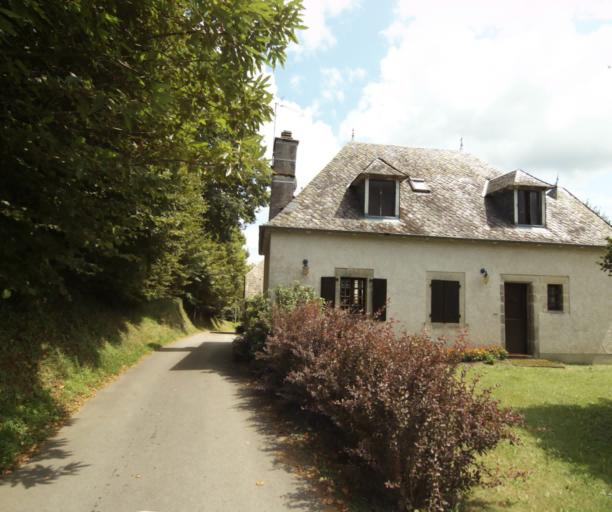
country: FR
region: Limousin
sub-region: Departement de la Correze
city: Sainte-Fortunade
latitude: 45.1914
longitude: 1.8318
